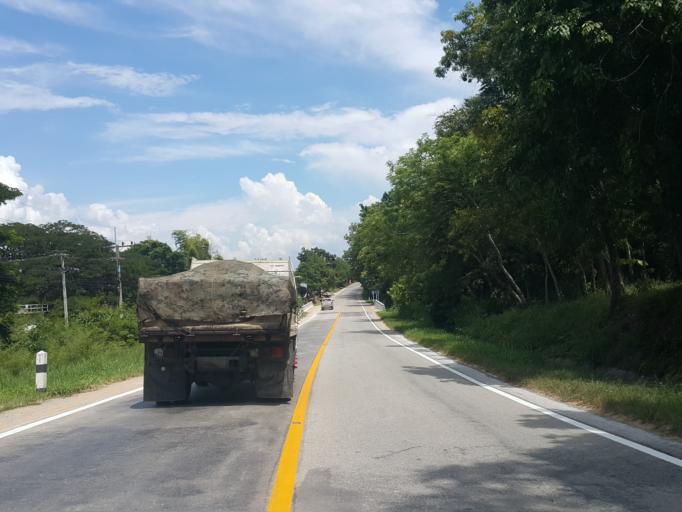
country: TH
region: Chiang Mai
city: Phrao
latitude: 19.2834
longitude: 99.1875
